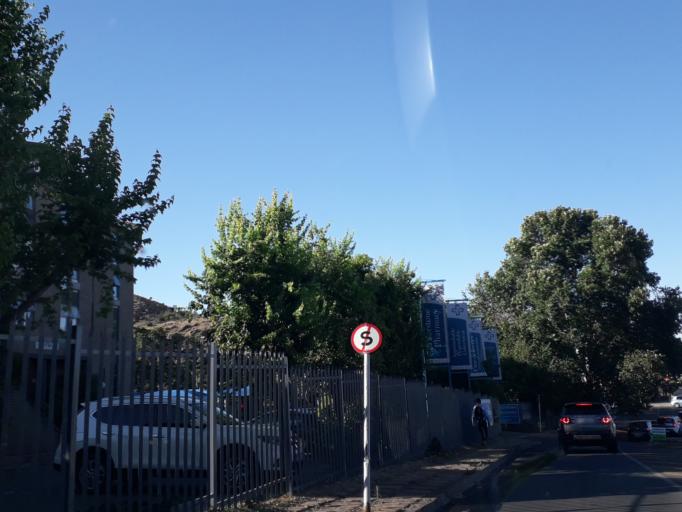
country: ZA
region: Gauteng
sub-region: City of Johannesburg Metropolitan Municipality
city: Roodepoort
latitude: -26.1510
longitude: 27.9209
